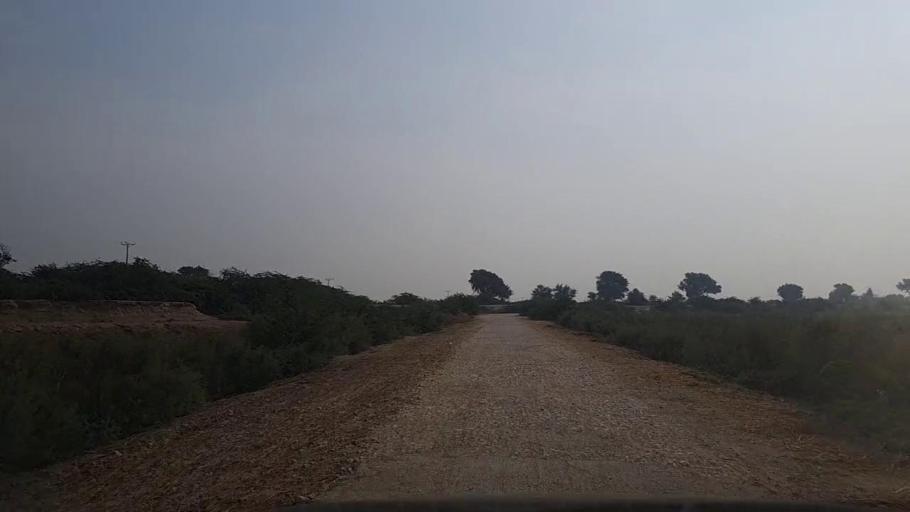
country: PK
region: Sindh
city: Mirpur Sakro
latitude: 24.3767
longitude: 67.7556
